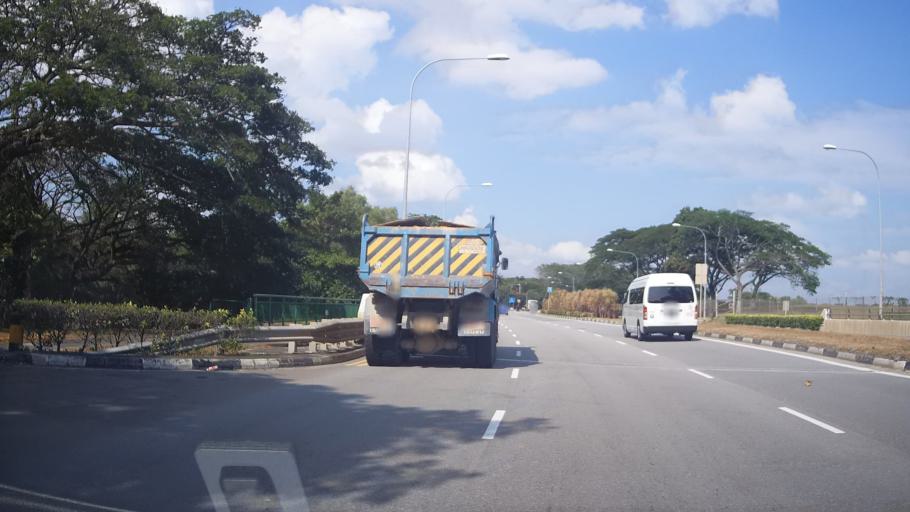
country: SG
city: Singapore
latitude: 1.3259
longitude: 103.9755
